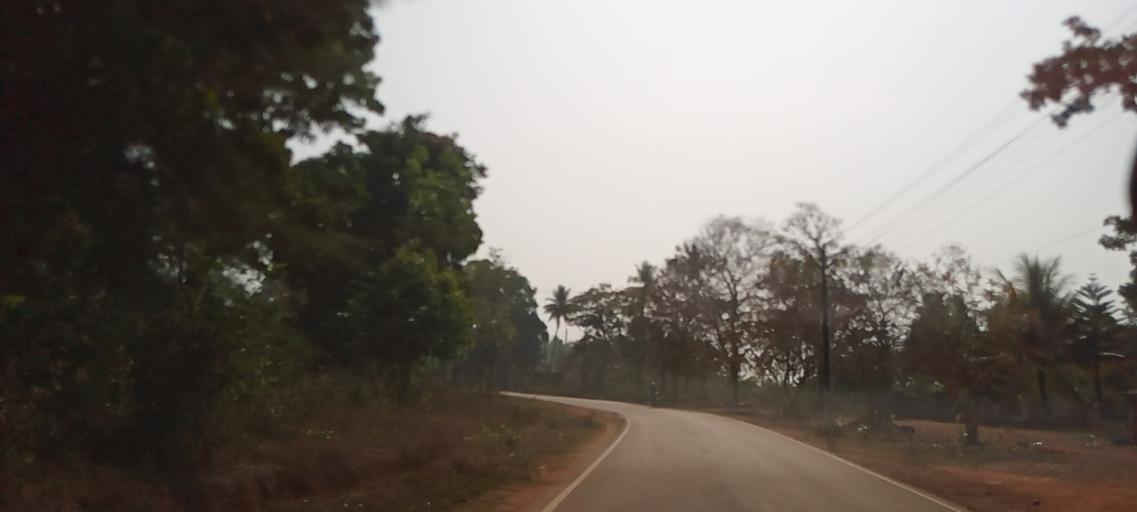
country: IN
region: Karnataka
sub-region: Udupi
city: Manipala
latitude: 13.5115
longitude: 74.8212
